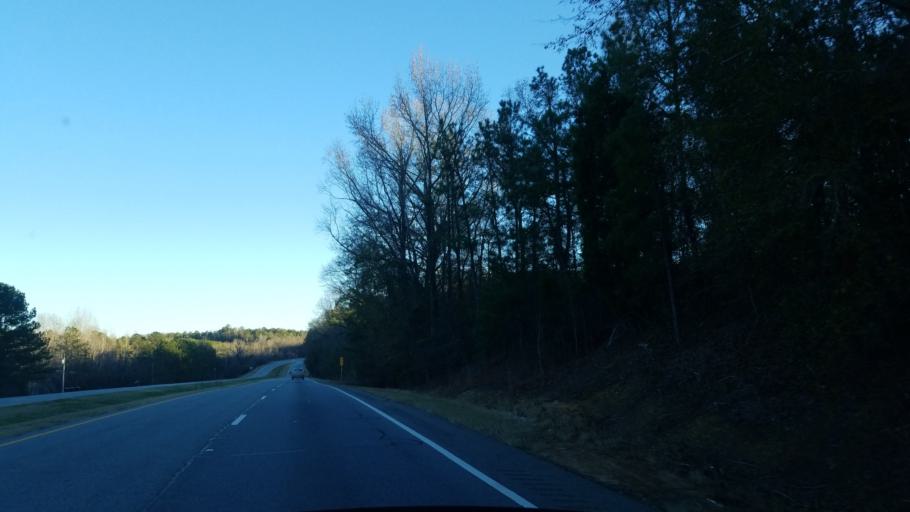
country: US
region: Georgia
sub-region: Chattahoochee County
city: Cusseta
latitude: 32.2618
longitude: -84.7325
